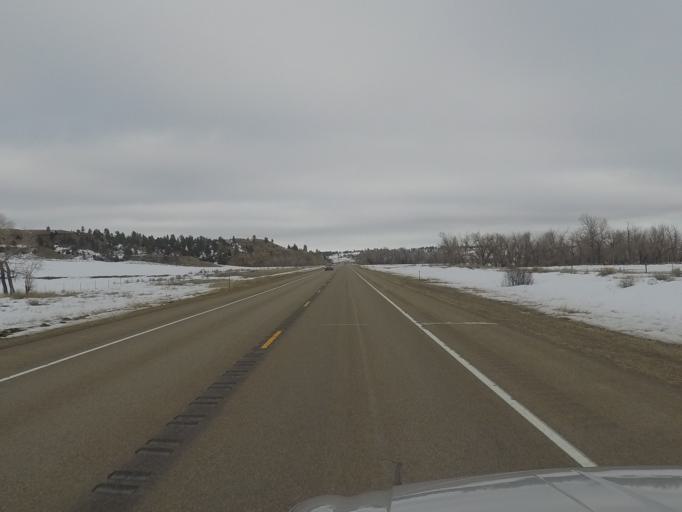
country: US
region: Montana
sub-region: Golden Valley County
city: Ryegate
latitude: 46.3085
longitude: -109.1234
